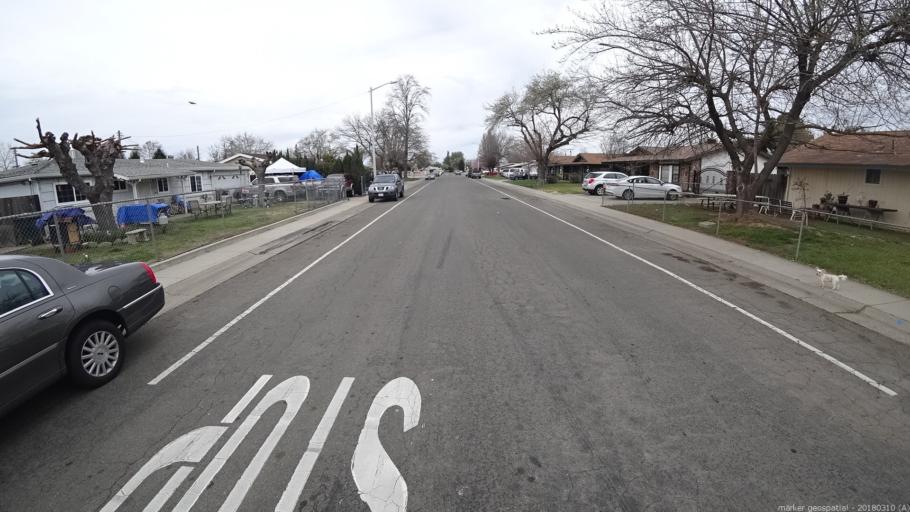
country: US
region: California
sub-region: Sacramento County
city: Florin
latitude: 38.4895
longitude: -121.4067
